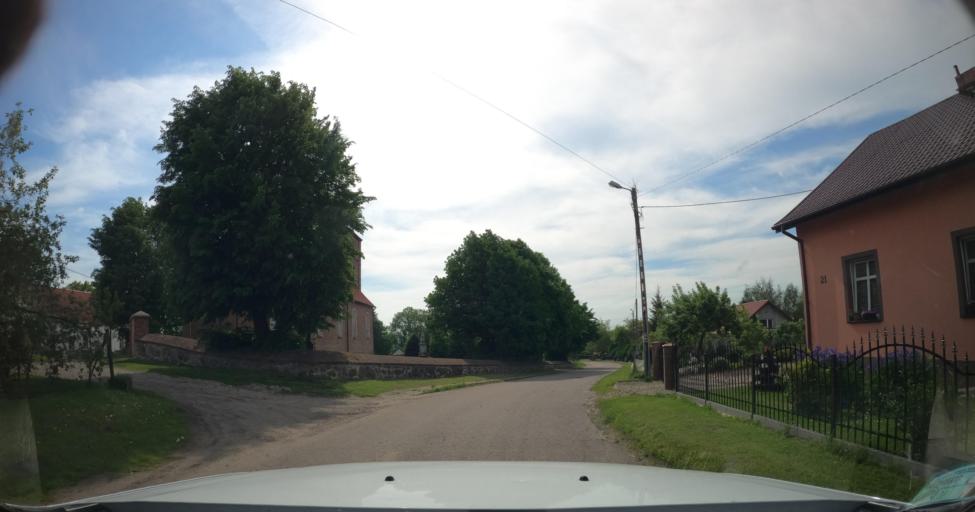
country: PL
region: Warmian-Masurian Voivodeship
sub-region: Powiat lidzbarski
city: Lubomino
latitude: 54.0889
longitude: 20.2972
